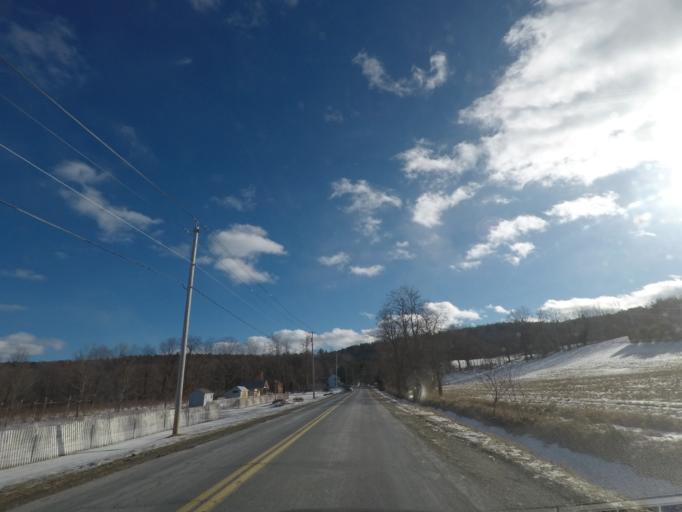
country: US
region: New York
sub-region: Rensselaer County
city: Hoosick Falls
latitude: 42.8327
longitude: -73.3902
